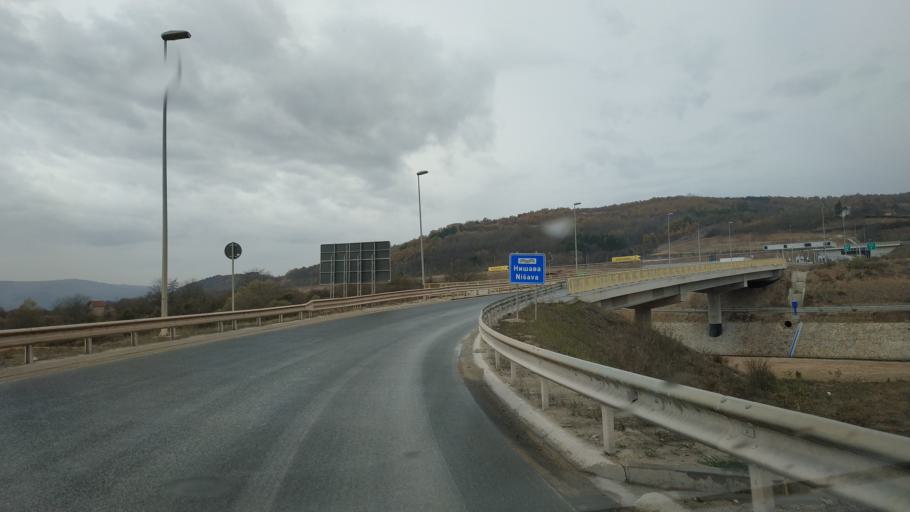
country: RS
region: Central Serbia
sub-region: Pirotski Okrug
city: Bela Palanka
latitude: 43.2319
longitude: 22.3174
